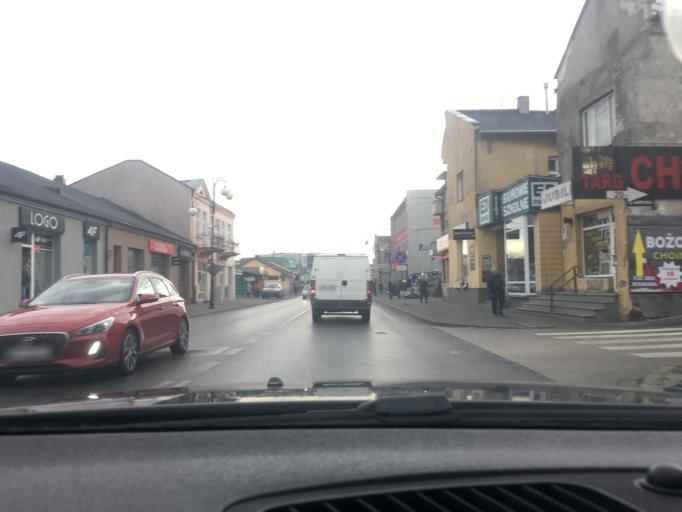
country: PL
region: Swietokrzyskie
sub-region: Powiat jedrzejowski
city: Jedrzejow
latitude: 50.6408
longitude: 20.3024
